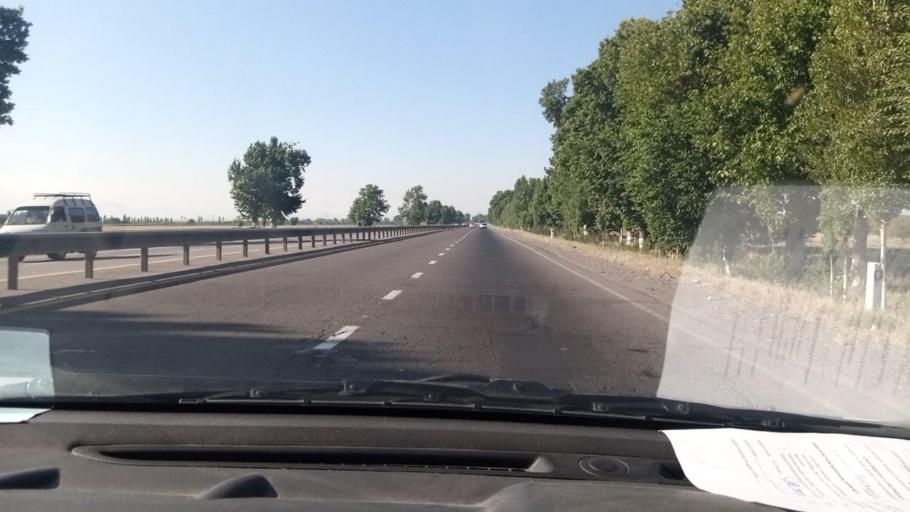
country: UZ
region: Toshkent Shahri
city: Bektemir
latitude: 41.2000
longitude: 69.4029
